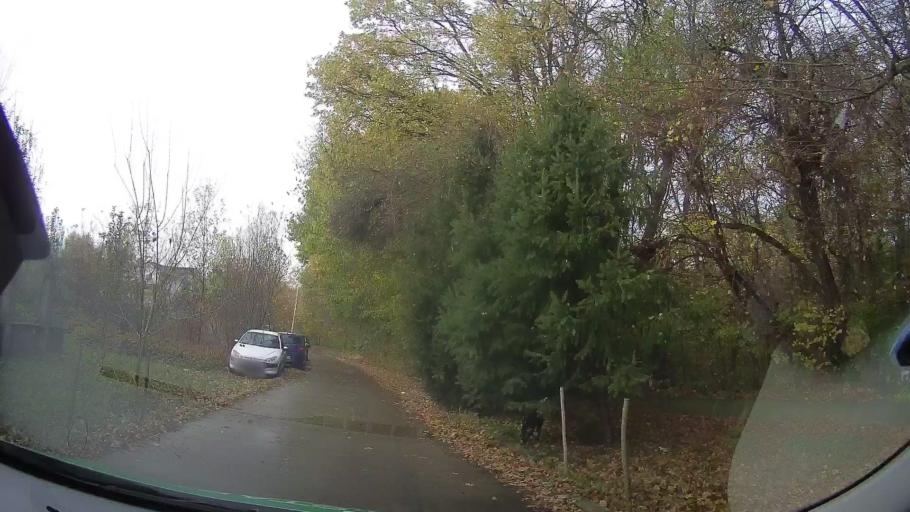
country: RO
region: Ilfov
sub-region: Comuna Snagov
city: Snagov
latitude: 44.7180
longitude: 26.1880
